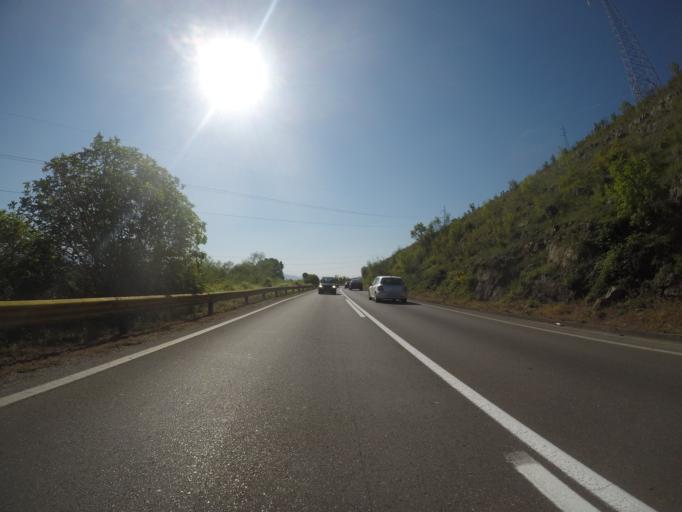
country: ME
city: Spuz
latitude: 42.4499
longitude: 19.1994
